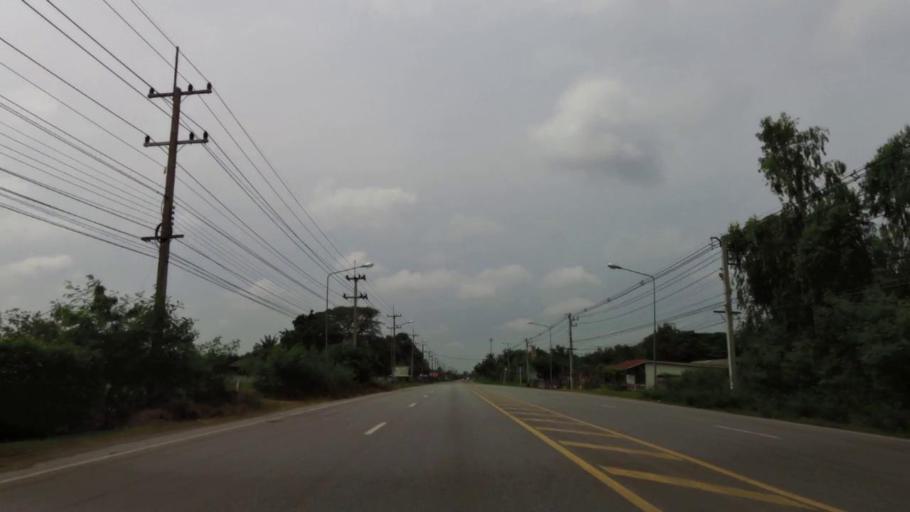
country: TH
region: Lop Buri
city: Ban Mi
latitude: 15.0648
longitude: 100.6208
